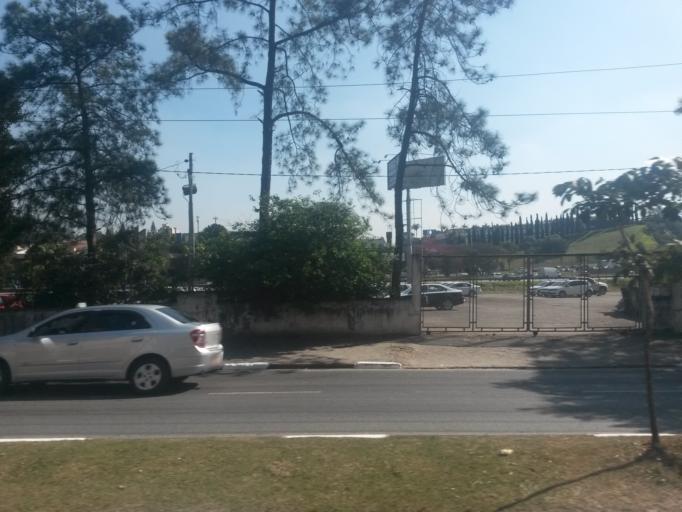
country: BR
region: Sao Paulo
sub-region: Sao Bernardo Do Campo
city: Sao Bernardo do Campo
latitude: -23.7265
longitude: -46.5491
